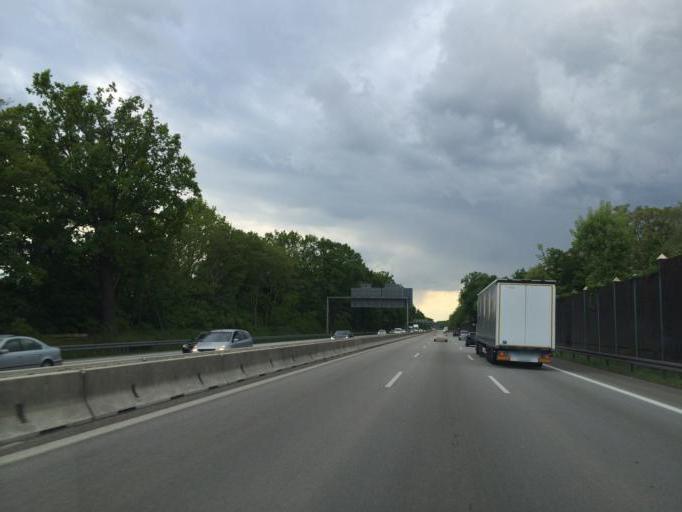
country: DE
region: Berlin
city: Grunewald
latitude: 52.4932
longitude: 13.2655
